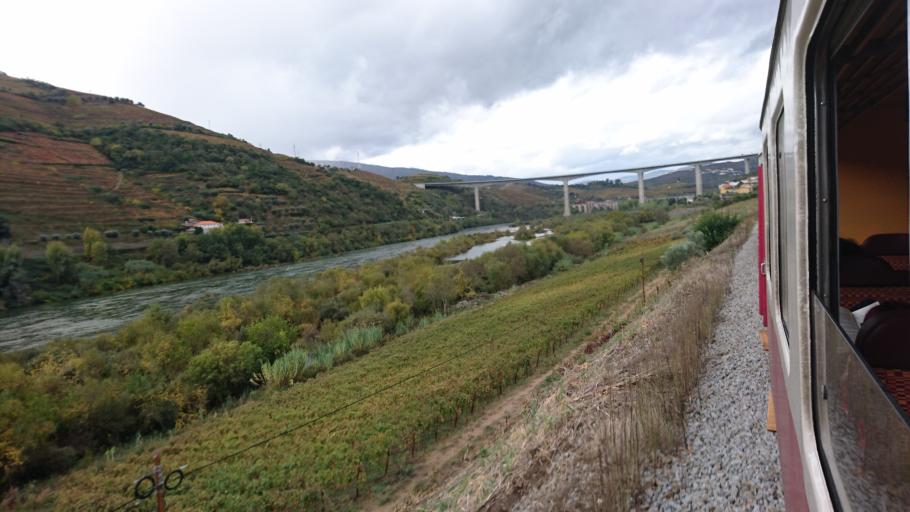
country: PT
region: Vila Real
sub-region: Peso da Regua
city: Peso da Regua
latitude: 41.1530
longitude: -7.7640
